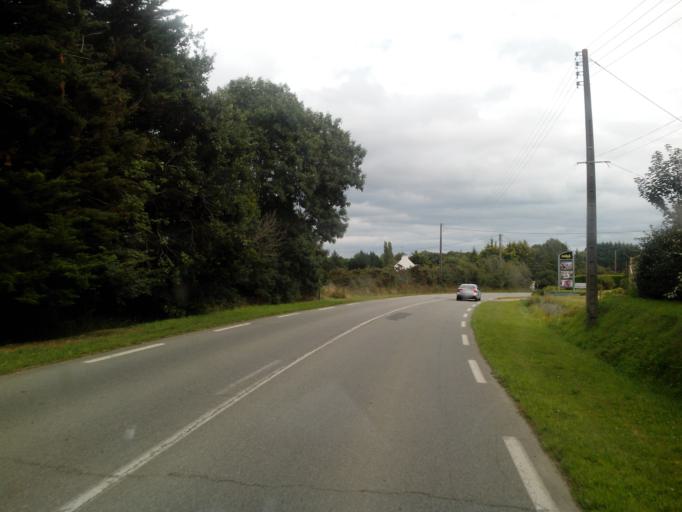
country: FR
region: Brittany
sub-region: Departement des Cotes-d'Armor
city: Plouha
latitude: 48.6680
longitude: -2.9124
